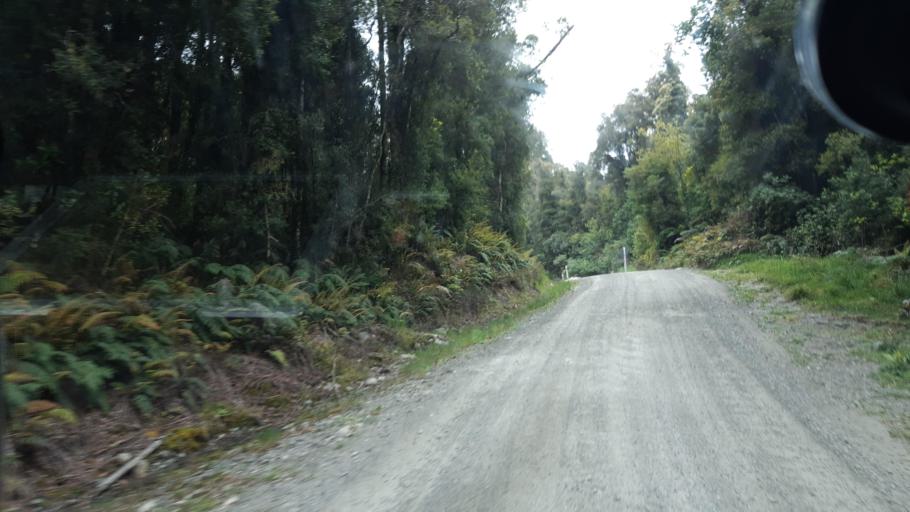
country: NZ
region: West Coast
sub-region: Grey District
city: Greymouth
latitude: -42.6476
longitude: 171.3578
